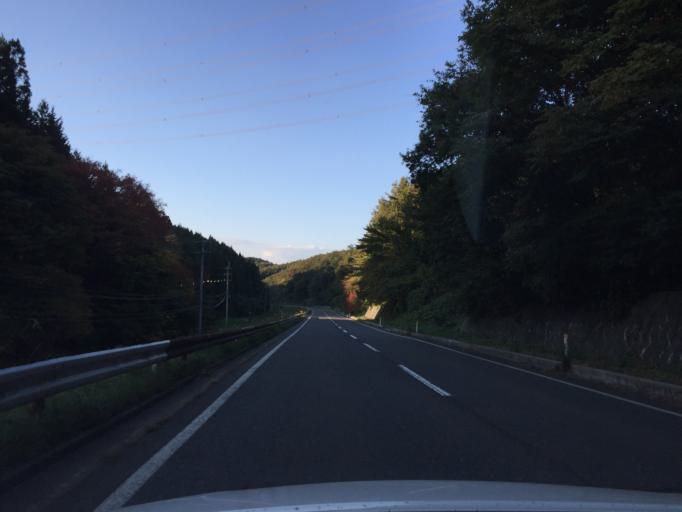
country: JP
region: Fukushima
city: Ishikawa
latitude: 37.1780
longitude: 140.6494
